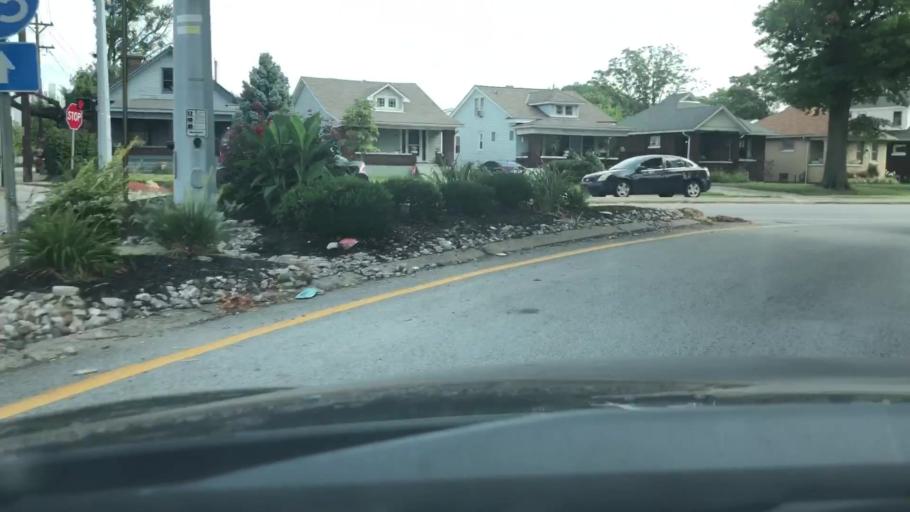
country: US
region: Kentucky
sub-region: Jefferson County
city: Audubon Park
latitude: 38.2114
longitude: -85.7512
